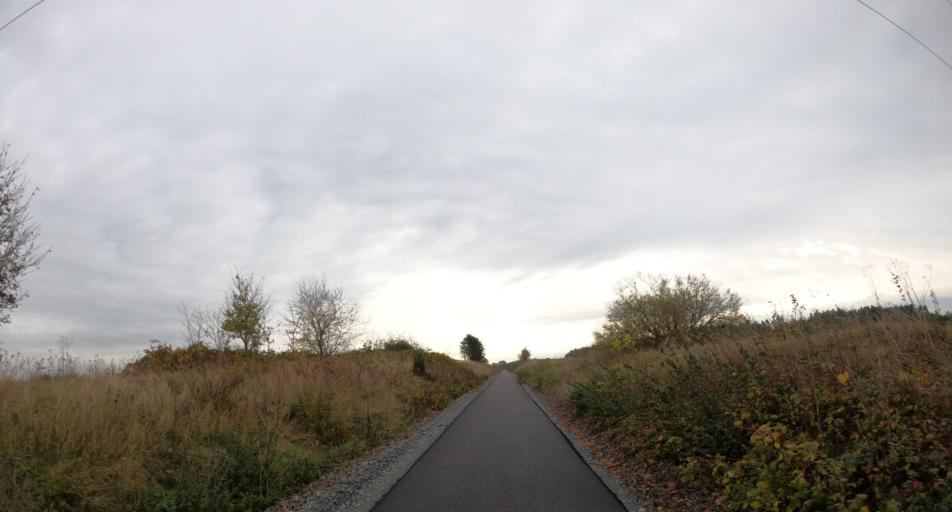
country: PL
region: West Pomeranian Voivodeship
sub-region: Powiat mysliborski
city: Nowogrodek Pomorski
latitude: 52.9873
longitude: 15.0707
